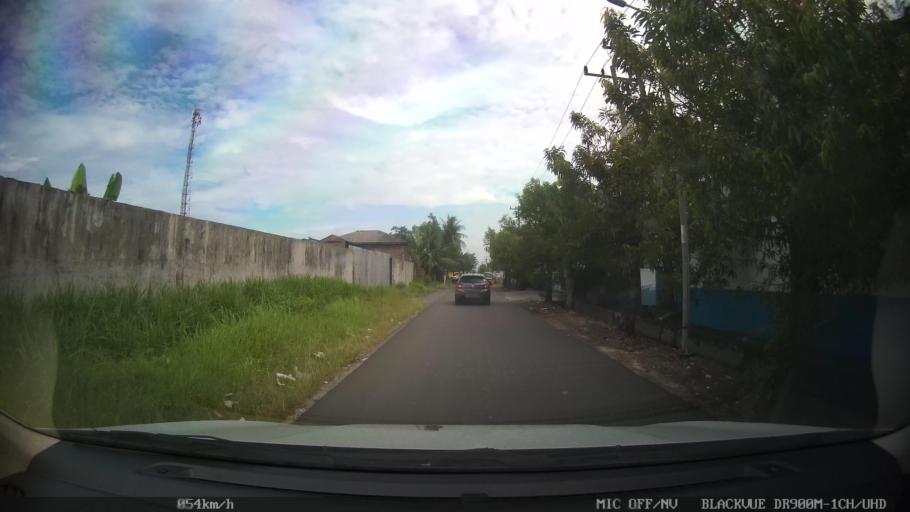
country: ID
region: North Sumatra
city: Sunggal
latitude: 3.5883
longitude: 98.5795
